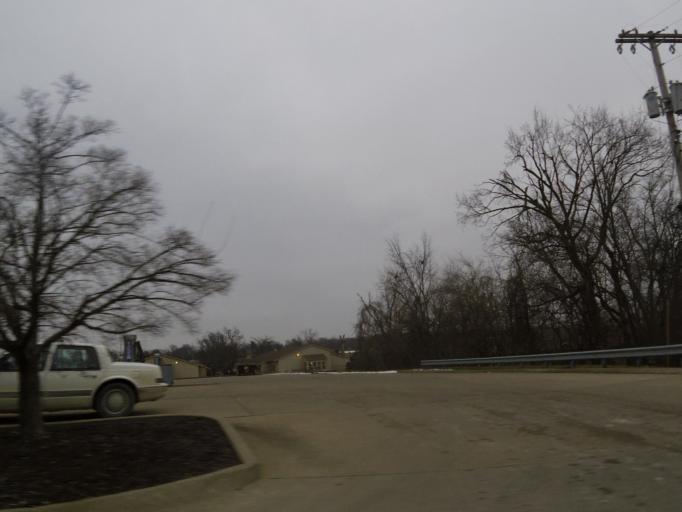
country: US
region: Missouri
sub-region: Marion County
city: Hannibal
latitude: 39.7266
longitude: -91.3963
